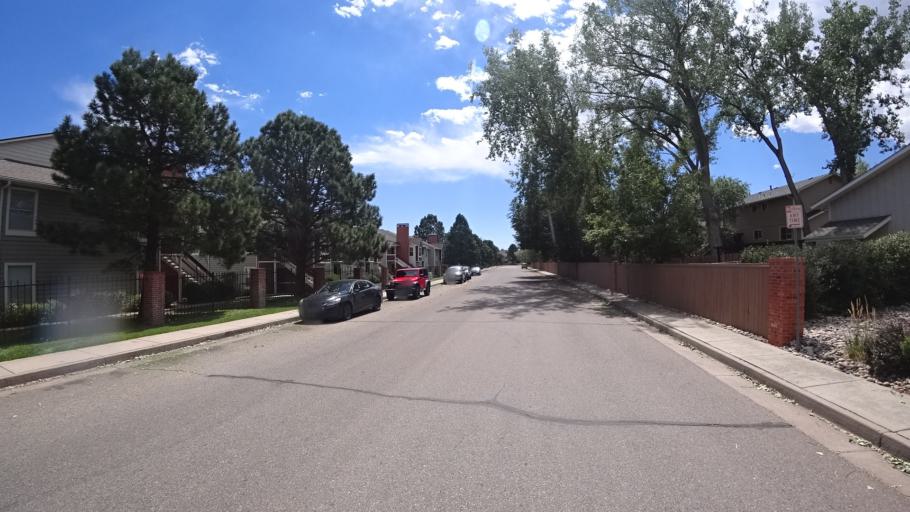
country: US
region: Colorado
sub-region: El Paso County
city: Stratmoor
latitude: 38.7740
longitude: -104.8162
